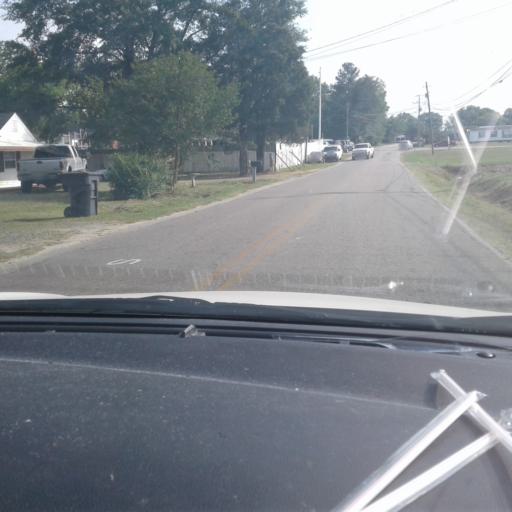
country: US
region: North Carolina
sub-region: Harnett County
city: Erwin
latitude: 35.3206
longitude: -78.6541
